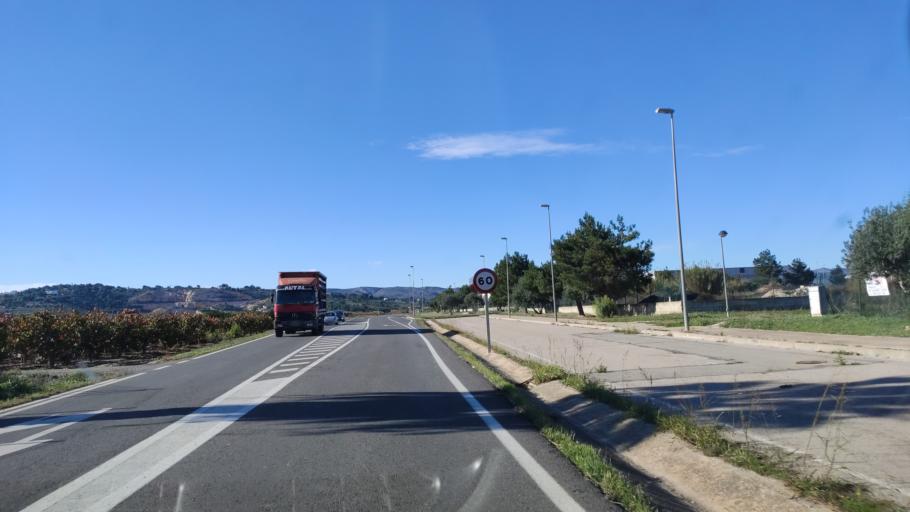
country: ES
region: Valencia
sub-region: Provincia de Valencia
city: Alberic
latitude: 39.1200
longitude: -0.5363
